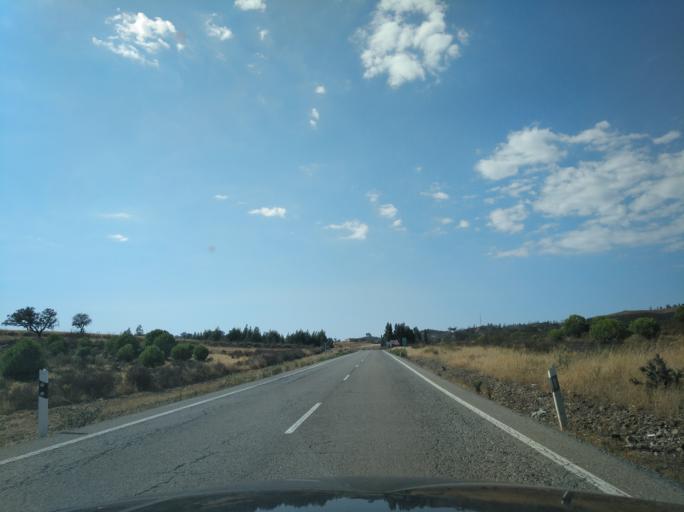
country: ES
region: Andalusia
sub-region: Provincia de Huelva
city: Santa Barbara de Casa
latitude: 37.7852
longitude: -7.1648
